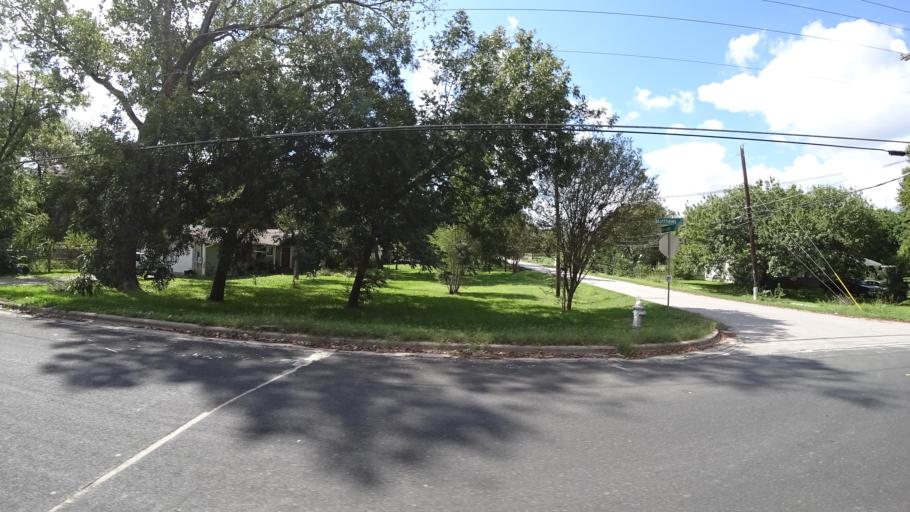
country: US
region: Texas
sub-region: Travis County
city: Onion Creek
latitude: 30.1959
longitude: -97.7987
